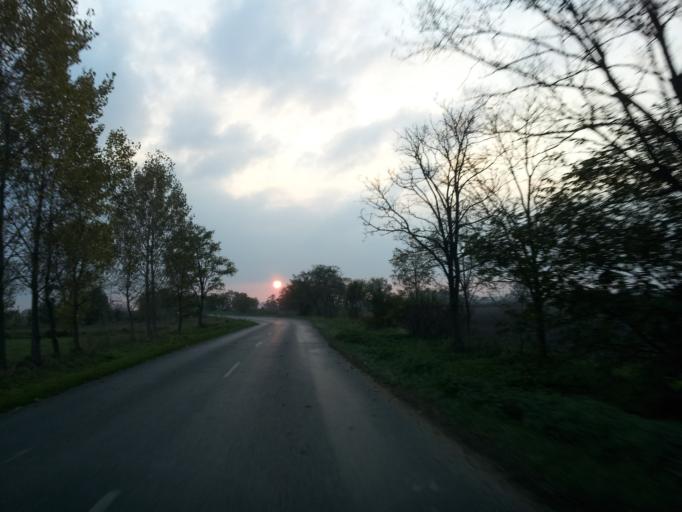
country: HU
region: Gyor-Moson-Sopron
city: Bakonyszentlaszlo
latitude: 47.4579
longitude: 17.8319
